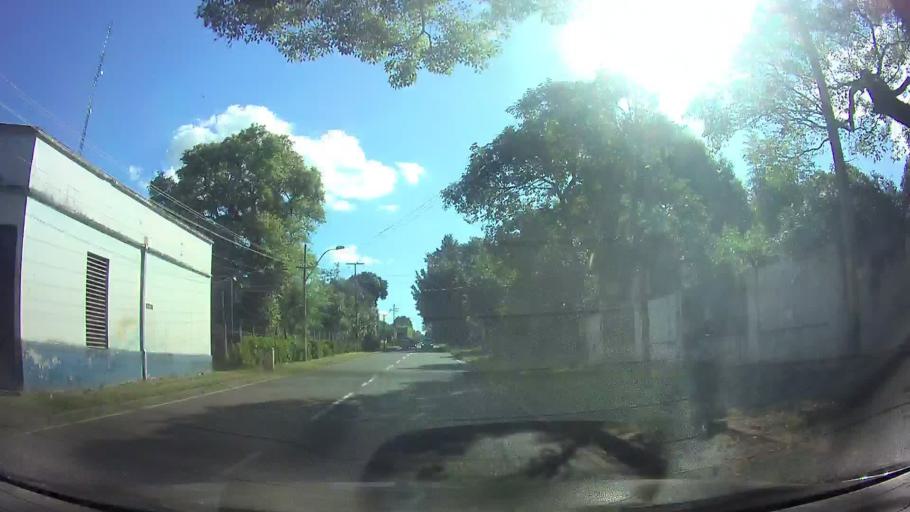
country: PY
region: Cordillera
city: Caacupe
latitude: -25.3920
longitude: -57.1412
